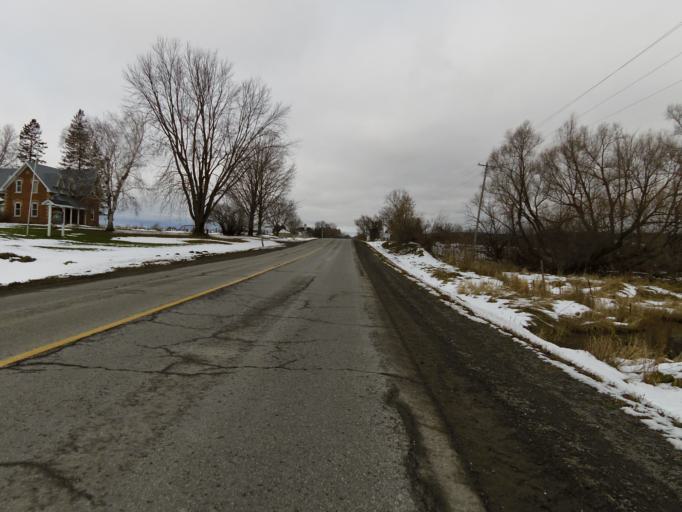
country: CA
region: Ontario
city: Bells Corners
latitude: 45.3412
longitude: -76.0551
